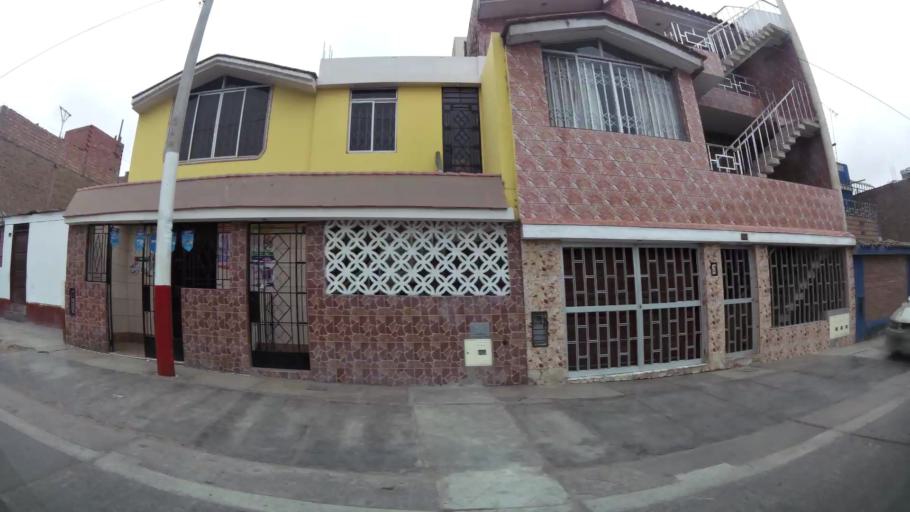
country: PE
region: Callao
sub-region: Callao
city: Callao
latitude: -12.0533
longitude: -77.1113
